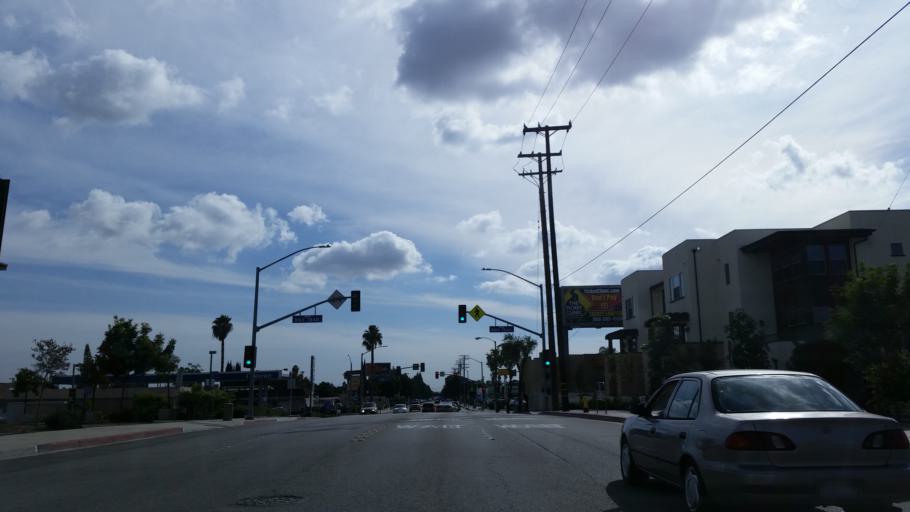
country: US
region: California
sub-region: Los Angeles County
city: Bellflower
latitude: 33.8906
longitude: -118.1340
